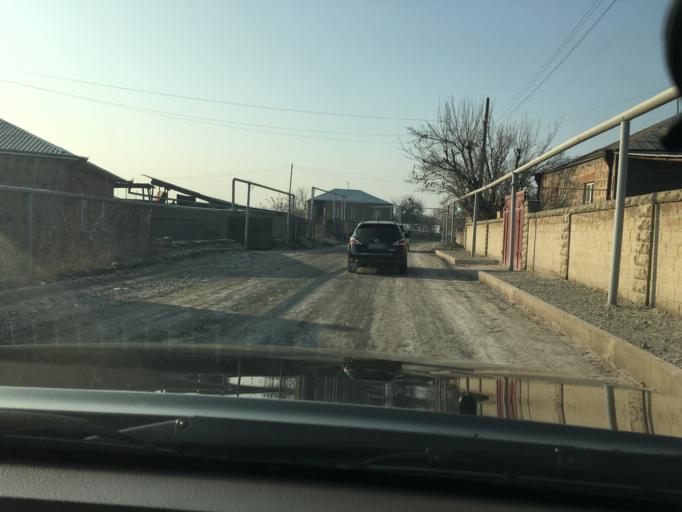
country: AM
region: Armavir
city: Janfida
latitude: 40.0450
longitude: 44.0292
